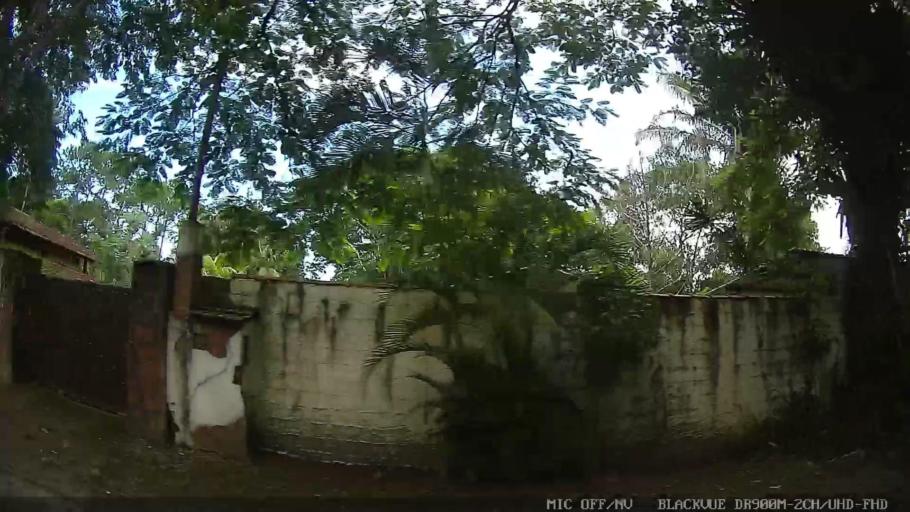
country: BR
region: Sao Paulo
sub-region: Iguape
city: Iguape
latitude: -24.6941
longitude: -47.5320
